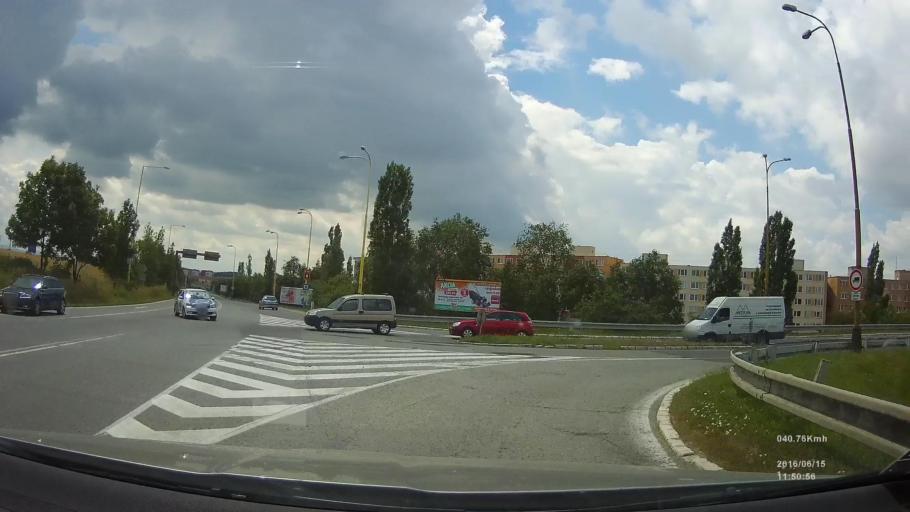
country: SK
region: Kosicky
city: Kosice
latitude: 48.7292
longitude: 21.2918
